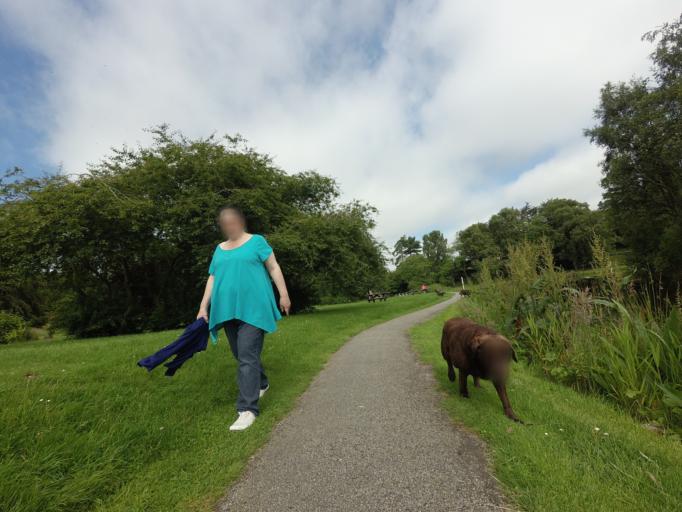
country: GB
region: Scotland
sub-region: Aberdeenshire
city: Turriff
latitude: 57.5341
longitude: -2.4607
